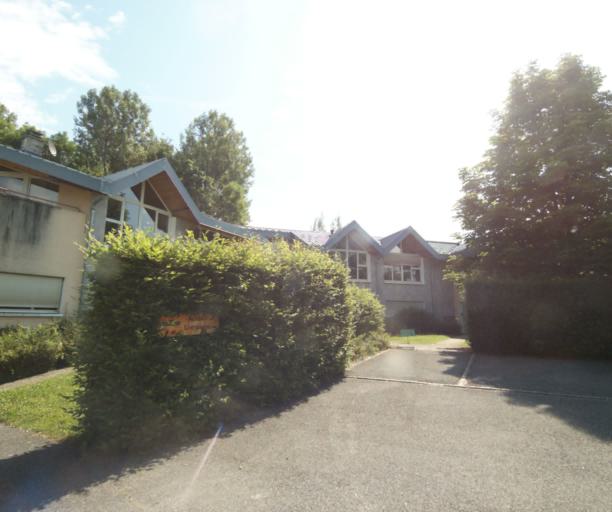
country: FR
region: Rhone-Alpes
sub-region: Departement de la Haute-Savoie
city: Allinges
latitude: 46.3356
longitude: 6.4855
